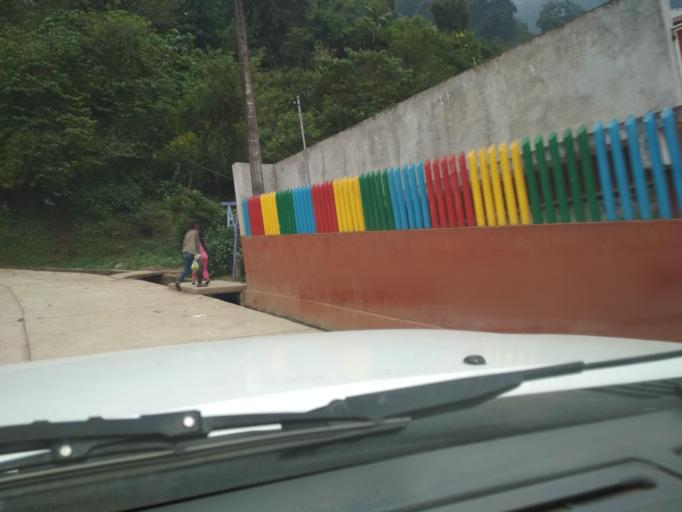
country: MX
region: Veracruz
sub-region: La Perla
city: Barrio de San Miguel
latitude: 18.9368
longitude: -97.1265
